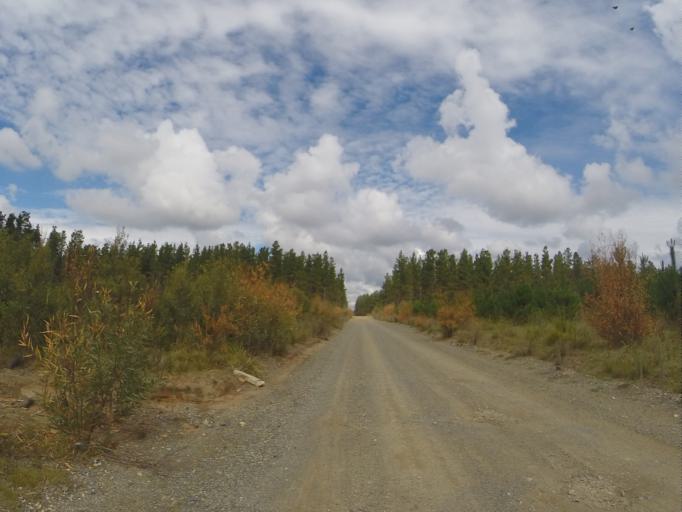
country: AU
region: New South Wales
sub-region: Wingecarribee
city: Moss Vale
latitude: -34.5260
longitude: 150.2283
